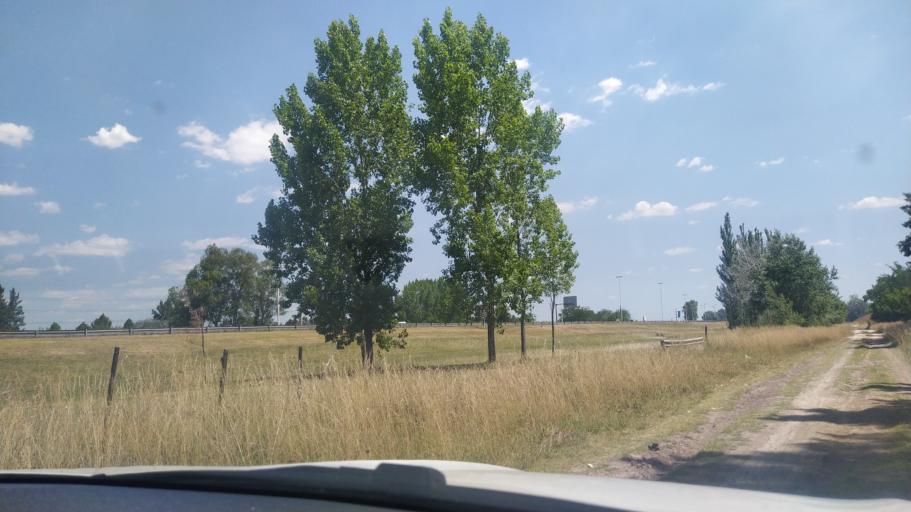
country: AR
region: Buenos Aires
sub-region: Partido de Ezeiza
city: Ezeiza
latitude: -34.9125
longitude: -58.6305
